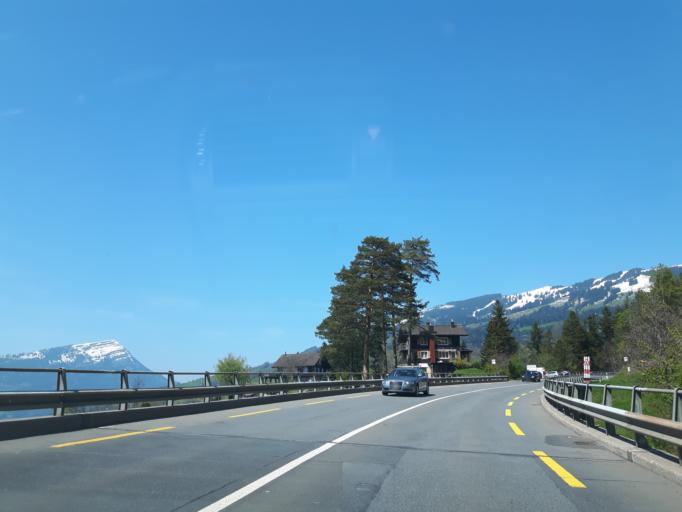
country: CH
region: Schwyz
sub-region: Bezirk Schwyz
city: Steinen
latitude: 47.0564
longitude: 8.6225
